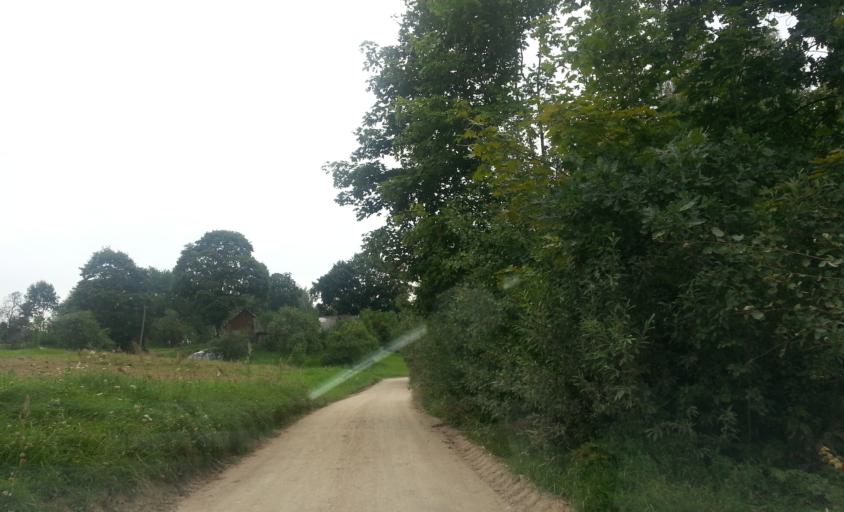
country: LT
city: Grigiskes
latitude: 54.7637
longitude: 25.0229
